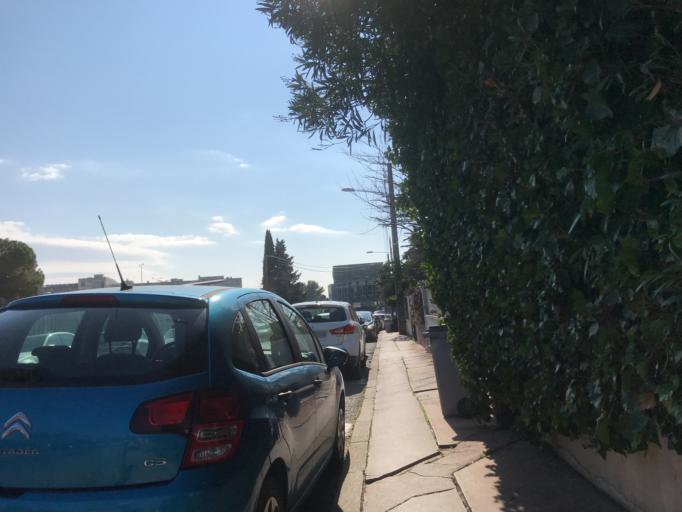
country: FR
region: Languedoc-Roussillon
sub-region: Departement de l'Herault
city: Montpellier
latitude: 43.6328
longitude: 3.8602
